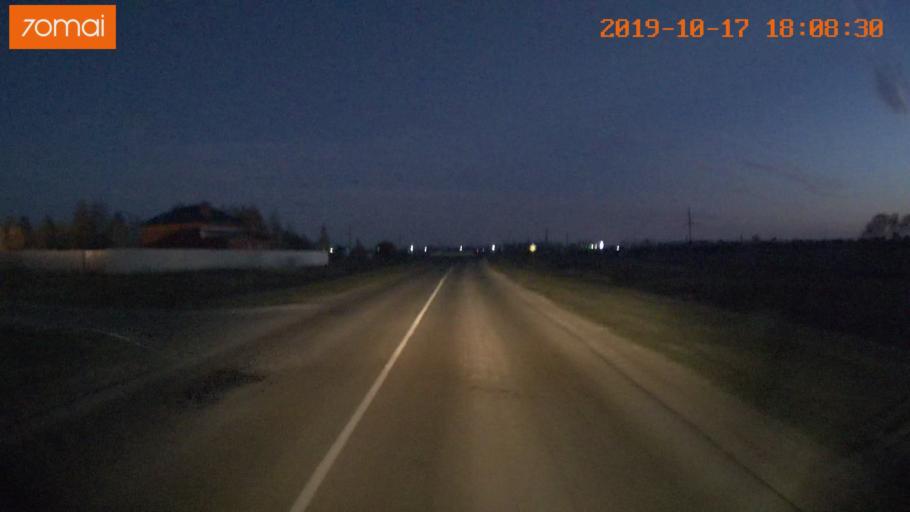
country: RU
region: Tula
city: Kurkino
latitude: 53.4333
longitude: 38.6436
